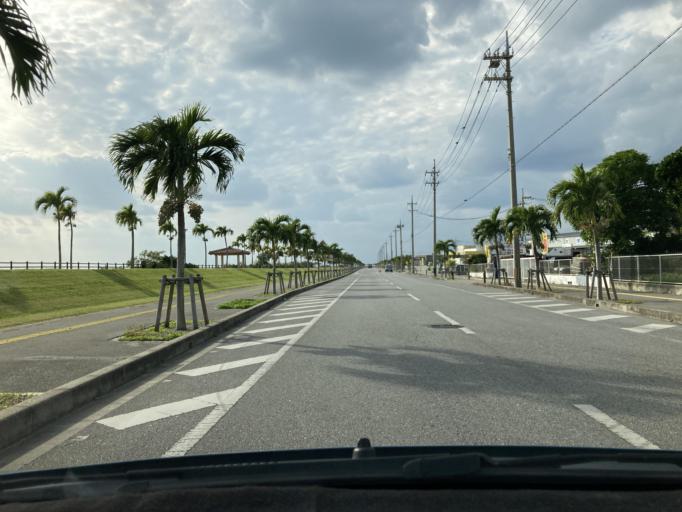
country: JP
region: Okinawa
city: Itoman
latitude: 26.1522
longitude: 127.6579
